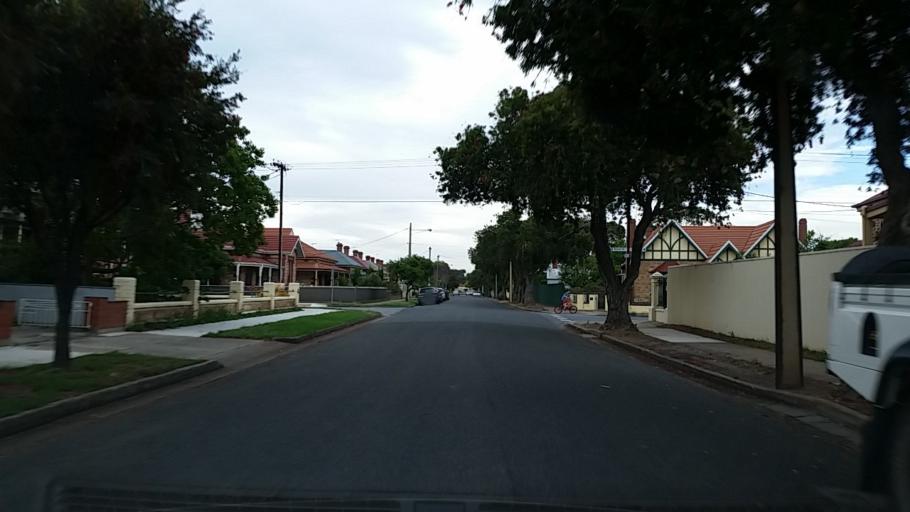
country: AU
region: South Australia
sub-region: Charles Sturt
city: Allenby Gardens
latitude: -34.9023
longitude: 138.5606
